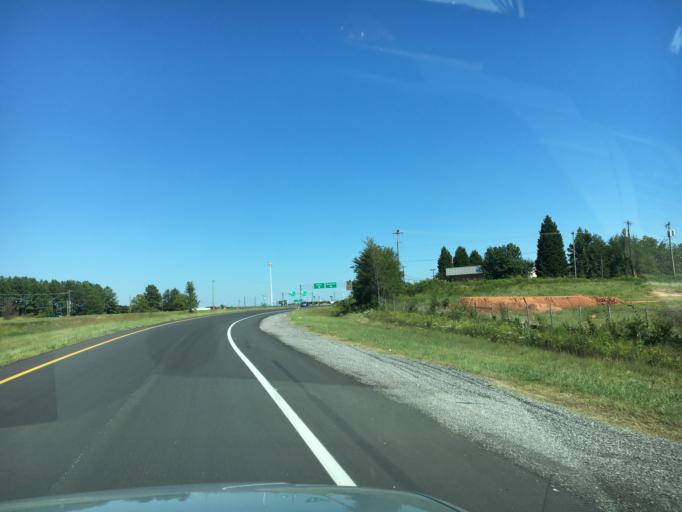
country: US
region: South Carolina
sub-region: Spartanburg County
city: Duncan
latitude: 34.8906
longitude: -82.1631
